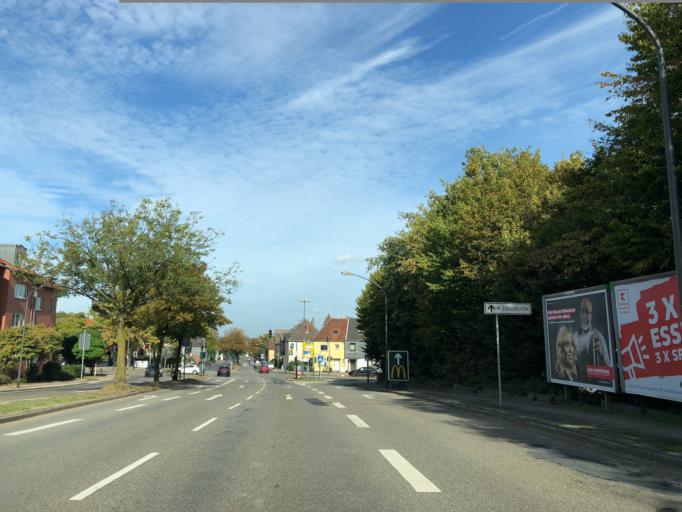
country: DE
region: North Rhine-Westphalia
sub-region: Regierungsbezirk Dusseldorf
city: Essen
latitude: 51.4584
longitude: 7.0335
